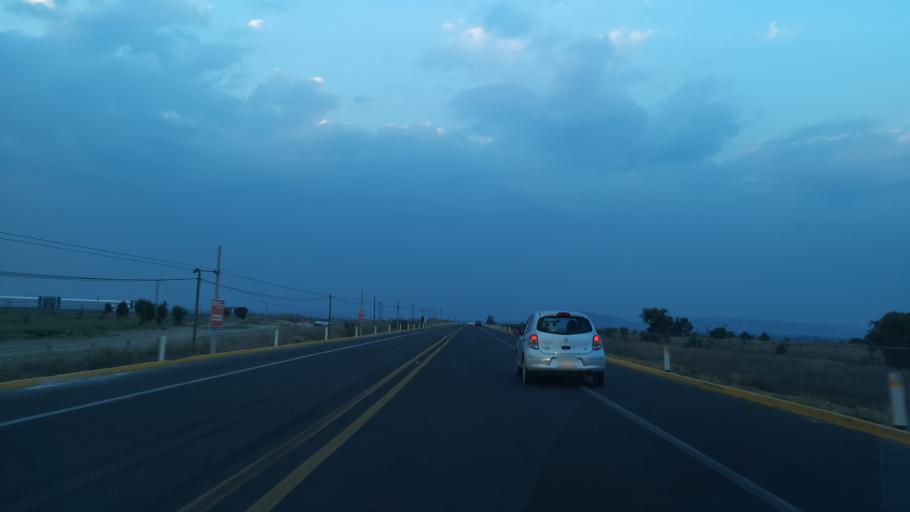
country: MX
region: Puebla
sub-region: Huejotzingo
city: Los Encinos
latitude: 19.1729
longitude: -98.3746
